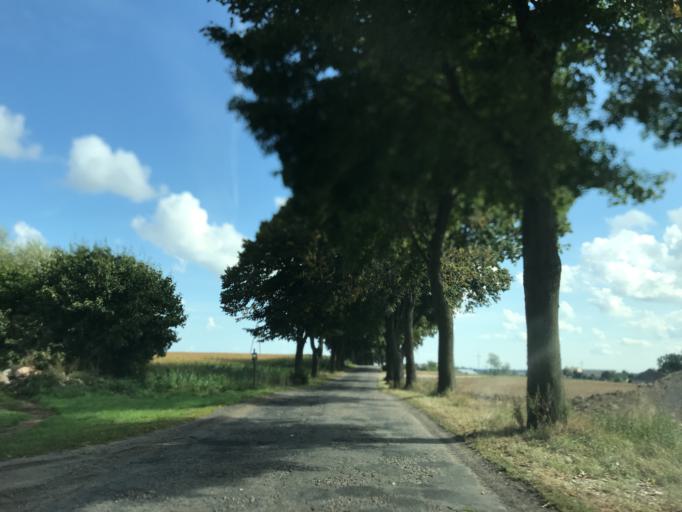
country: PL
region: Kujawsko-Pomorskie
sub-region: Powiat brodnicki
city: Brzozie
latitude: 53.3507
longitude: 19.6550
